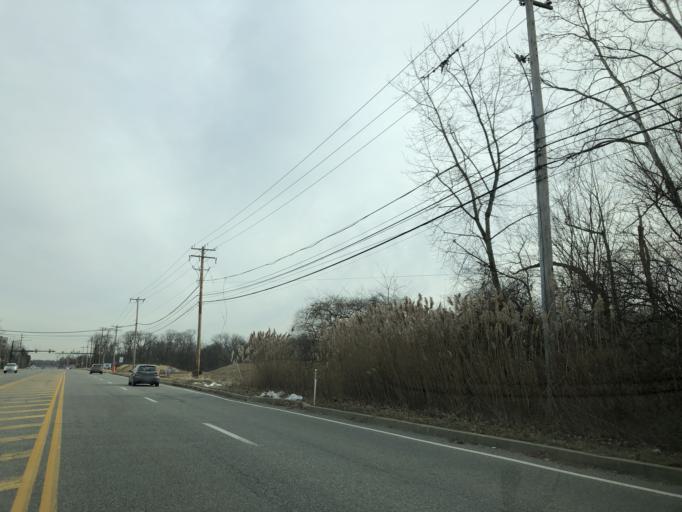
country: US
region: Pennsylvania
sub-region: Chester County
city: Exton
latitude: 40.0256
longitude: -75.6407
